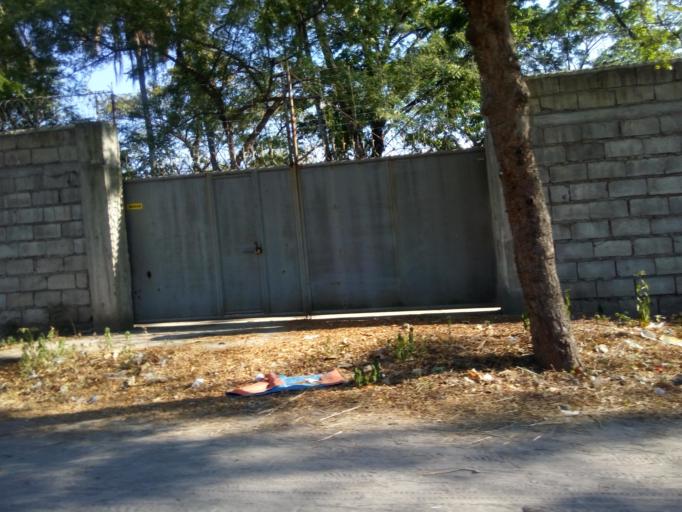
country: PH
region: Central Visayas
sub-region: Province of Negros Oriental
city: Valencia
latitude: 9.3129
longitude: 123.2644
